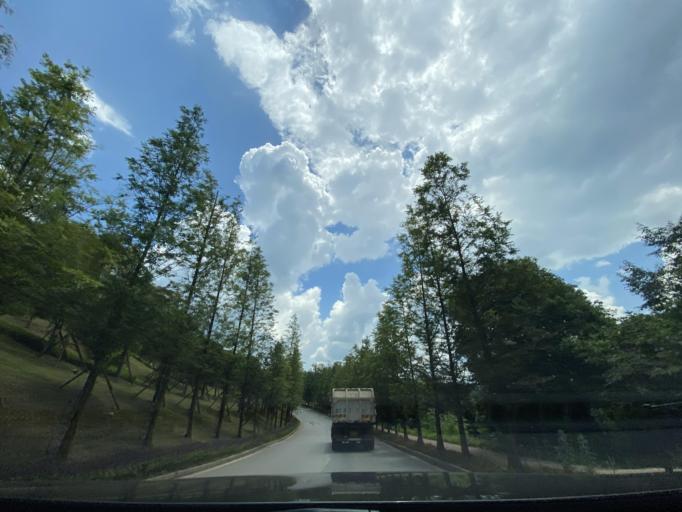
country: CN
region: Guizhou Sheng
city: Changqi
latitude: 28.5325
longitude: 105.9688
